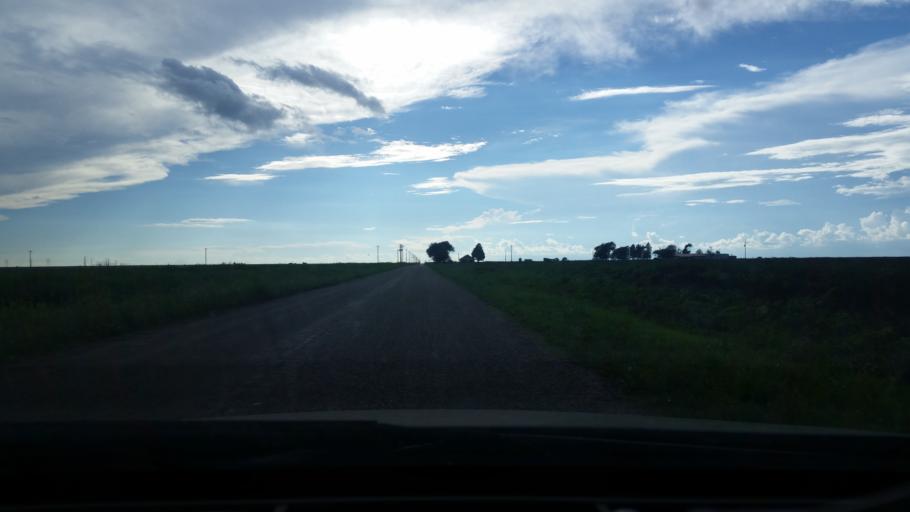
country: US
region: New Mexico
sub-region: Curry County
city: Clovis
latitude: 34.4630
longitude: -103.2273
